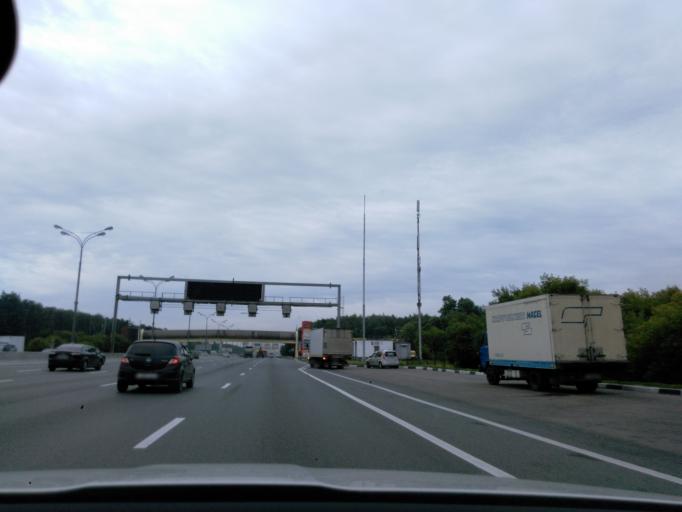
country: RU
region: Moscow
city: Zhulebino
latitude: 55.6700
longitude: 37.8366
